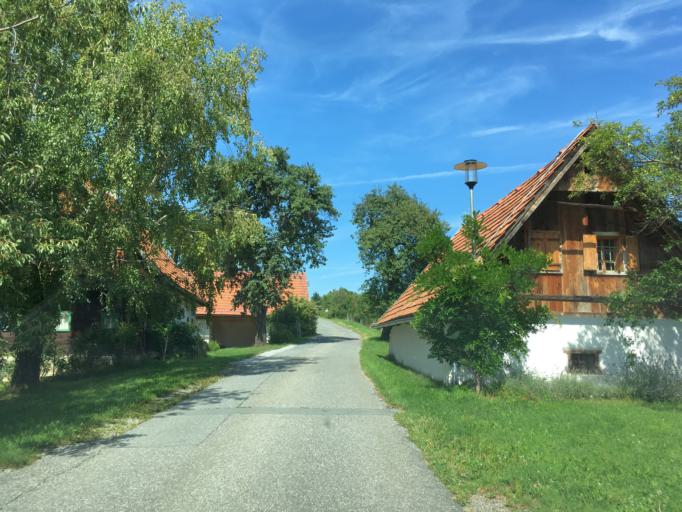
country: AT
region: Styria
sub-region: Politischer Bezirk Leibnitz
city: Kitzeck im Sausal
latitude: 46.7869
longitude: 15.4218
